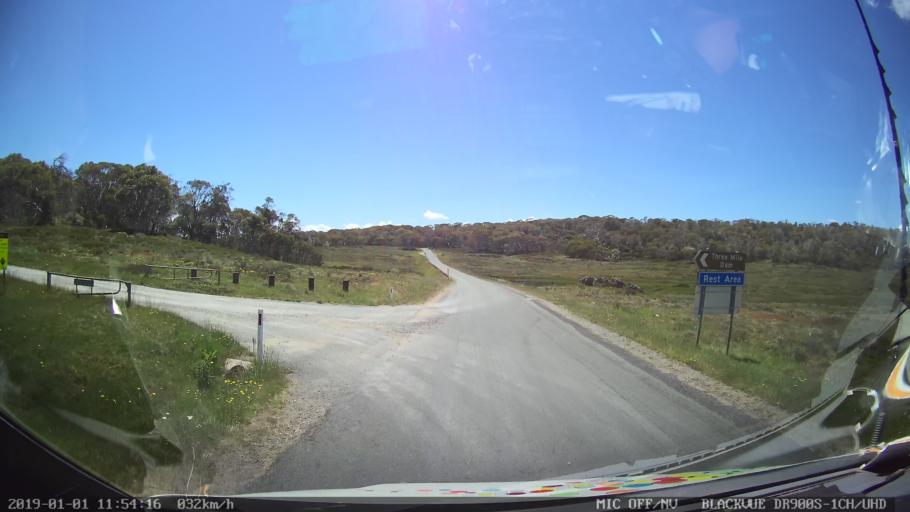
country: AU
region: New South Wales
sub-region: Snowy River
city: Jindabyne
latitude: -35.8917
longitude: 148.4480
